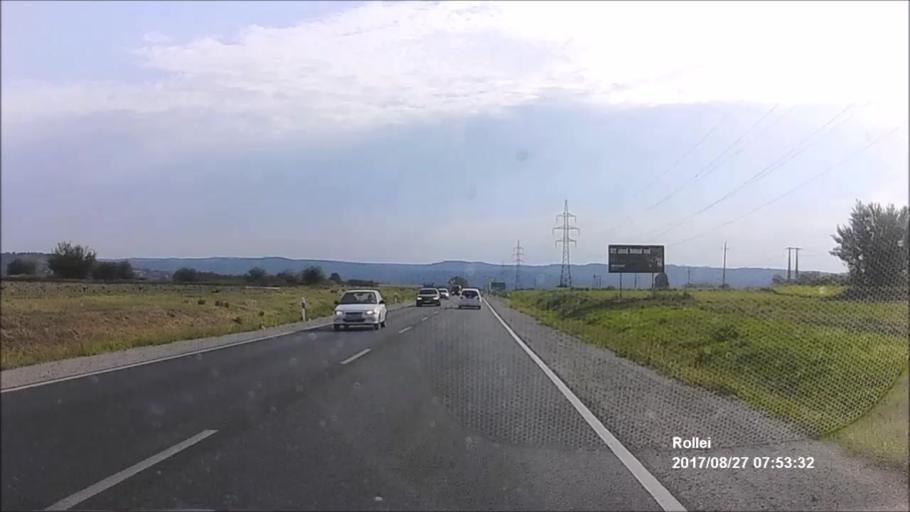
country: HU
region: Zala
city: Keszthely
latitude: 46.7807
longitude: 17.2336
